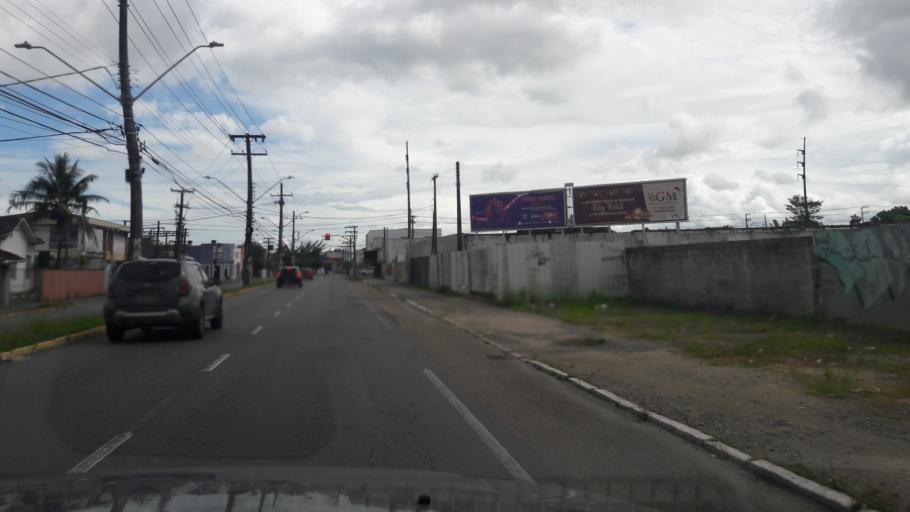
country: BR
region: Santa Catarina
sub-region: Joinville
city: Joinville
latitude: -26.3177
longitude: -48.8405
